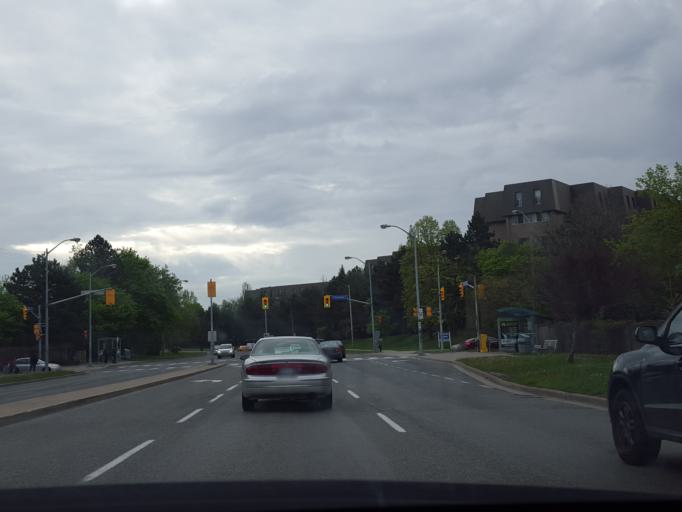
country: CA
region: Ontario
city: Willowdale
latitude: 43.7940
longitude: -79.3379
